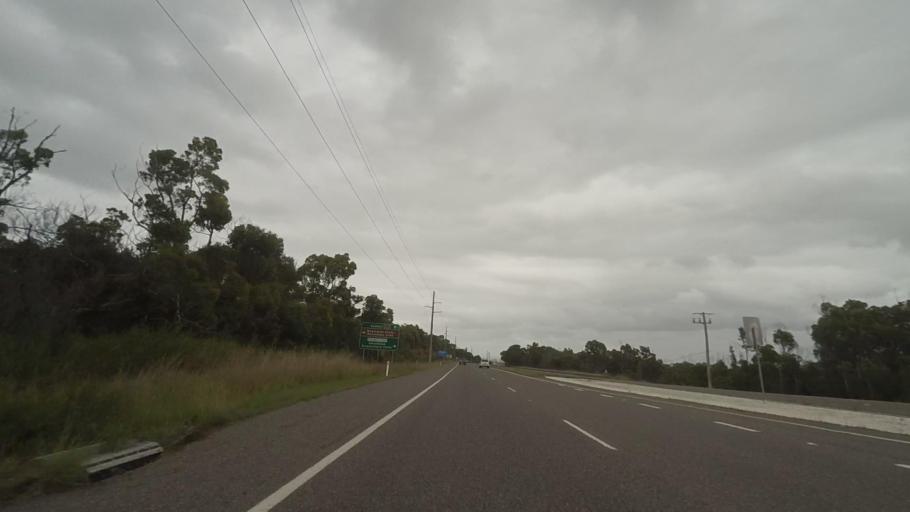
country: AU
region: New South Wales
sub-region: Wyong Shire
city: Kingfisher Shores
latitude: -33.1790
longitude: 151.5990
